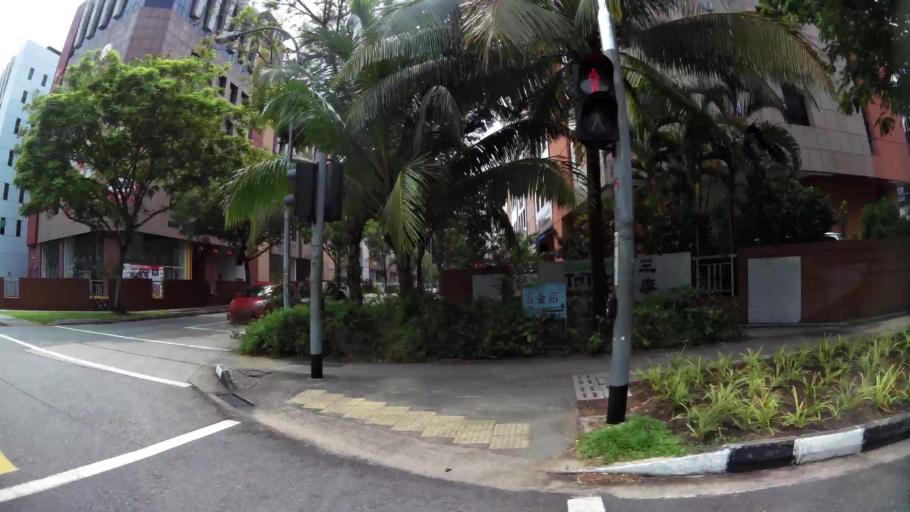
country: SG
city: Singapore
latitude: 1.3361
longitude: 103.9044
